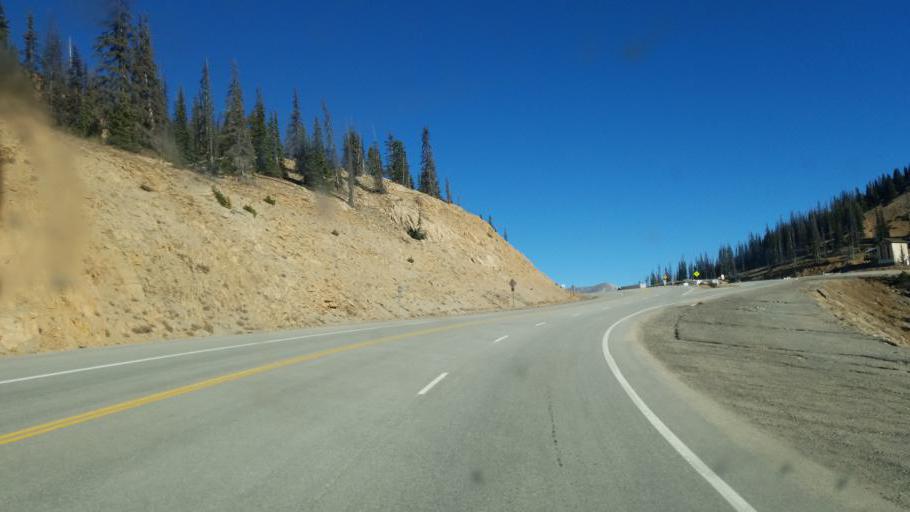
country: US
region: Colorado
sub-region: Chaffee County
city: Salida
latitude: 38.4935
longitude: -106.3269
